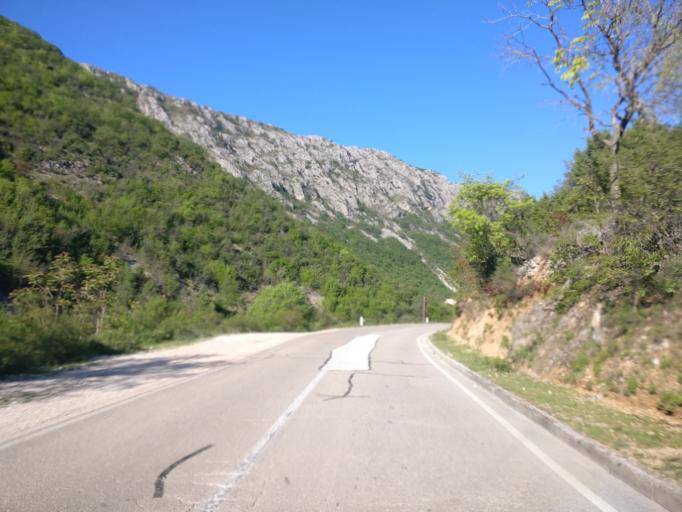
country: BA
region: Federation of Bosnia and Herzegovina
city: Stolac
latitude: 43.0722
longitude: 18.0427
